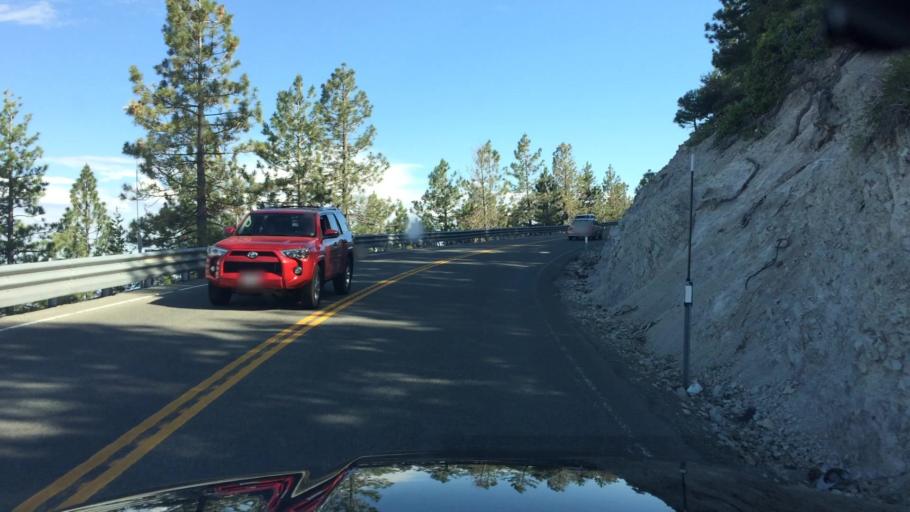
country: US
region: Nevada
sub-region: Washoe County
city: Incline Village
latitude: 39.3363
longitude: -119.8682
